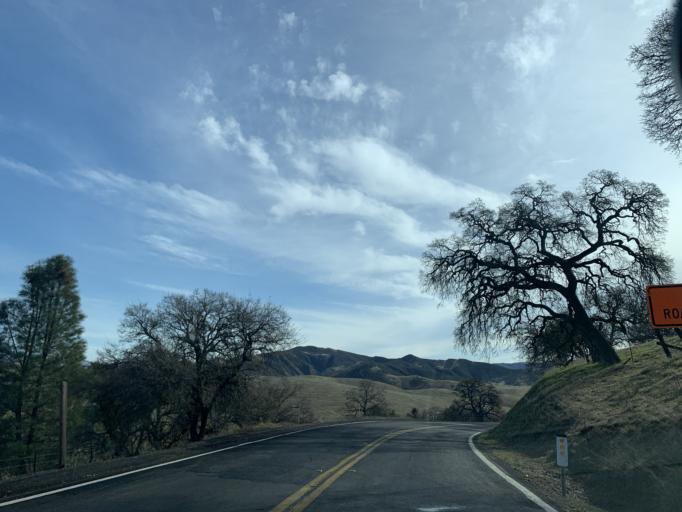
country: US
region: California
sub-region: Monterey County
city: Greenfield
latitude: 36.5076
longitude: -121.0946
